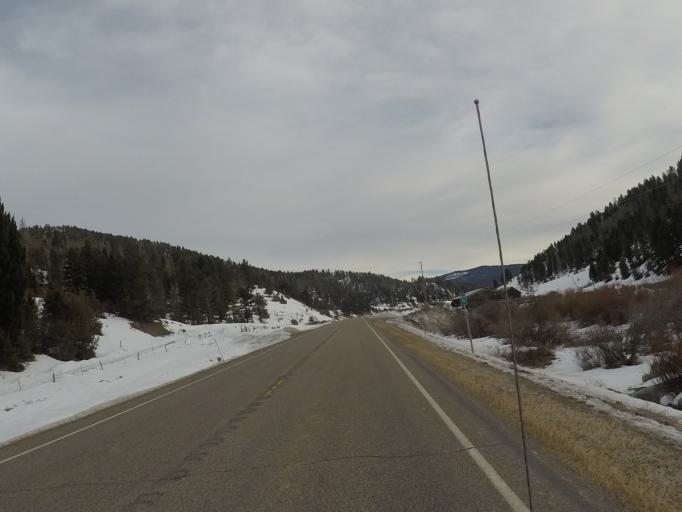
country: US
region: Montana
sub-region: Meagher County
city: White Sulphur Springs
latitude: 46.6850
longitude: -110.8742
